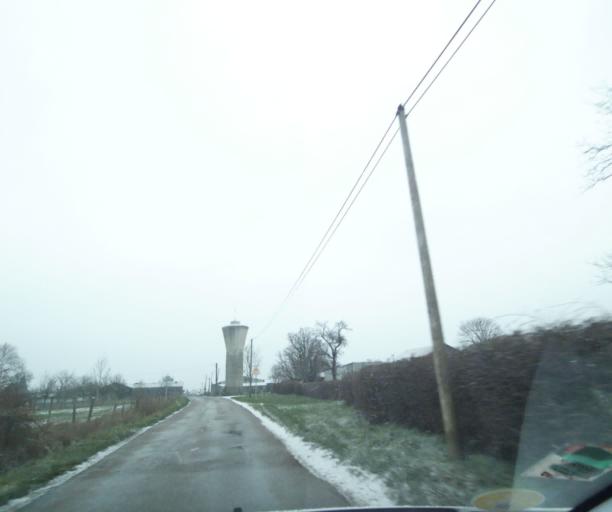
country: FR
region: Champagne-Ardenne
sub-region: Departement de la Haute-Marne
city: Wassy
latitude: 48.4694
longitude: 5.0360
